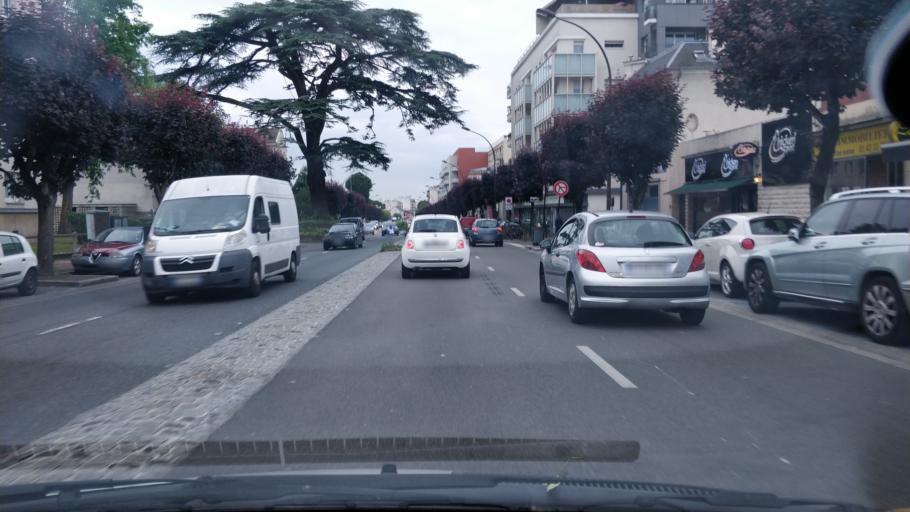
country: FR
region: Ile-de-France
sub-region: Departement de Seine-Saint-Denis
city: Livry-Gargan
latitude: 48.9219
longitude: 2.5424
